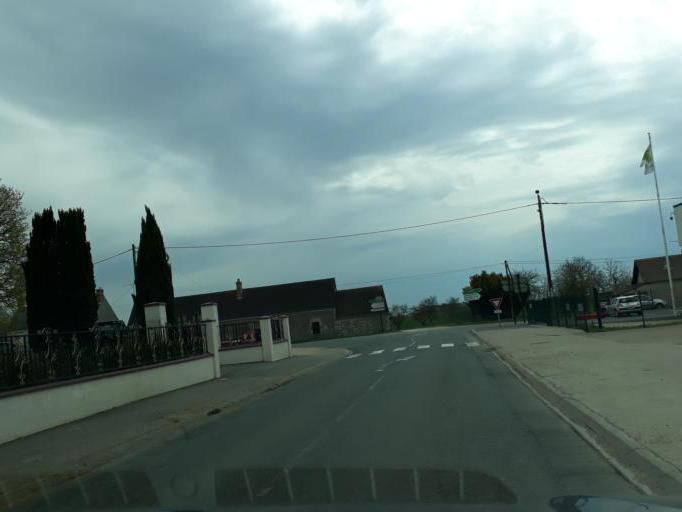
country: FR
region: Centre
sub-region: Departement du Loiret
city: Epieds-en-Beauce
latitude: 47.9394
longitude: 1.6220
